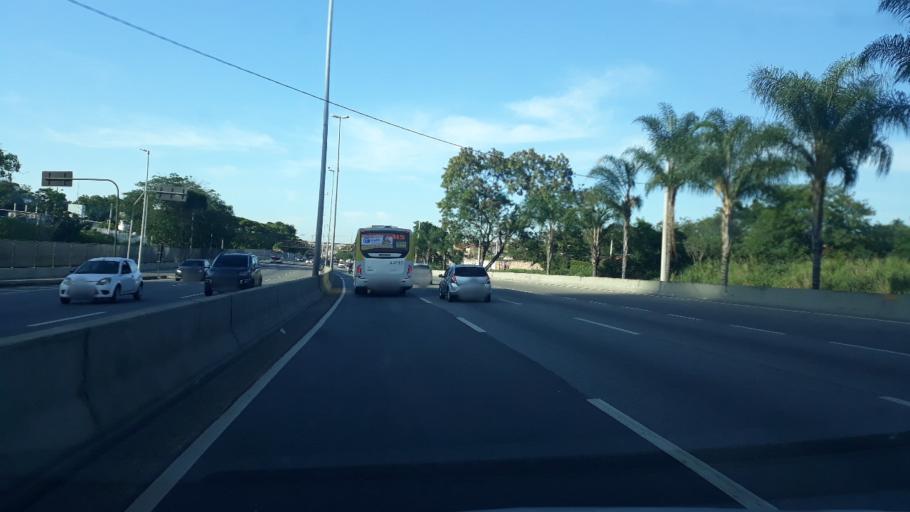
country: BR
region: Rio de Janeiro
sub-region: Sao Joao De Meriti
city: Sao Joao de Meriti
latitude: -22.9411
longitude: -43.3517
